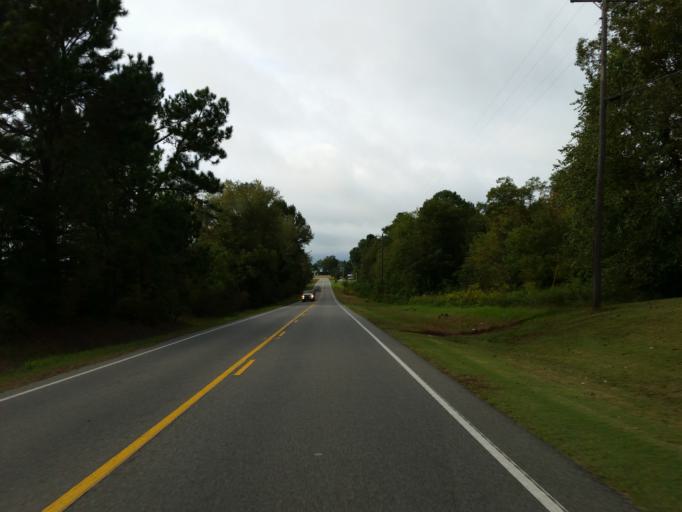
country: US
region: Georgia
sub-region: Turner County
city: Ashburn
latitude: 31.5835
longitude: -83.5736
